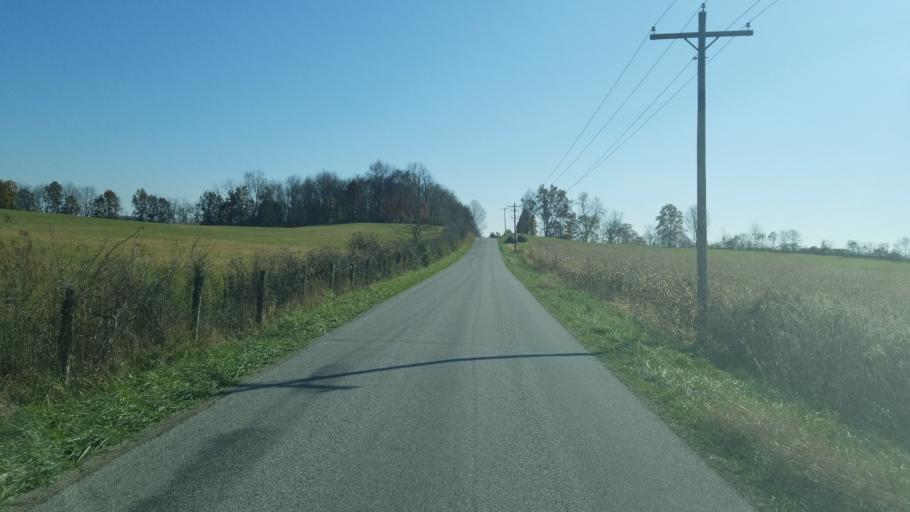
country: US
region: Ohio
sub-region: Licking County
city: Newark
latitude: 40.1266
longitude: -82.3900
